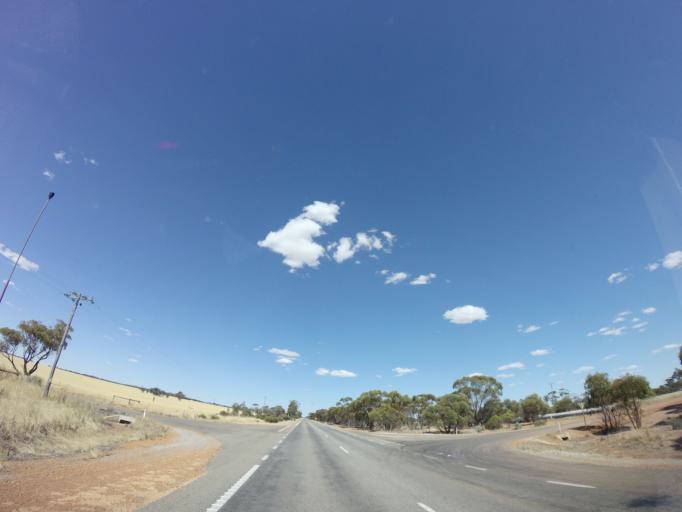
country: AU
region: Western Australia
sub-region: Cunderdin
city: Cunderdin
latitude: -31.6250
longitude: 117.5763
